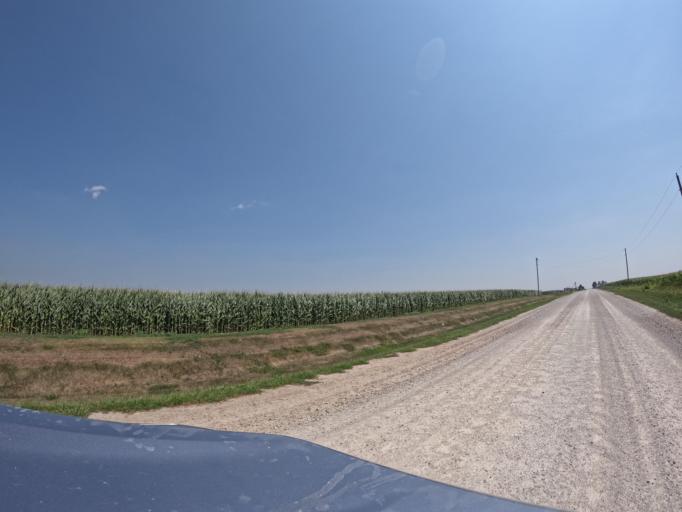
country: US
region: Iowa
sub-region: Keokuk County
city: Sigourney
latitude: 41.3437
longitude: -92.2387
